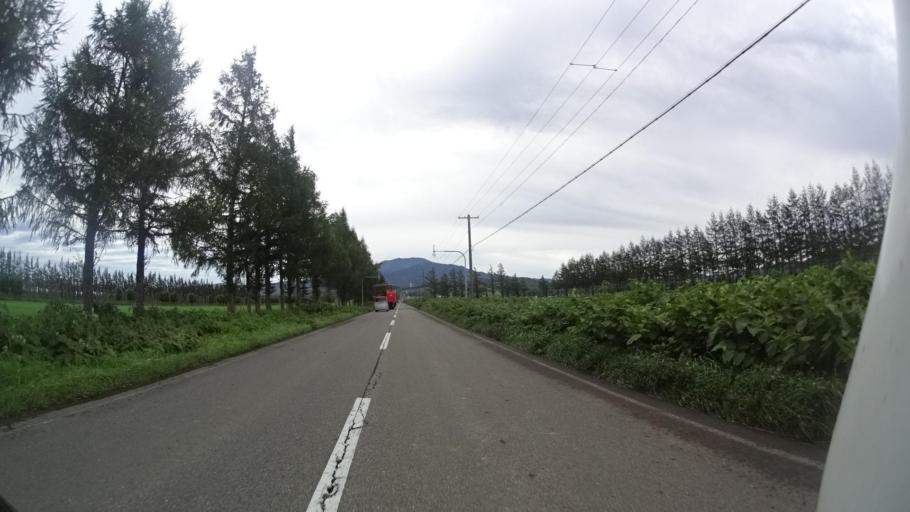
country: JP
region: Hokkaido
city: Shibetsu
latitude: 43.8739
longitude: 144.7338
